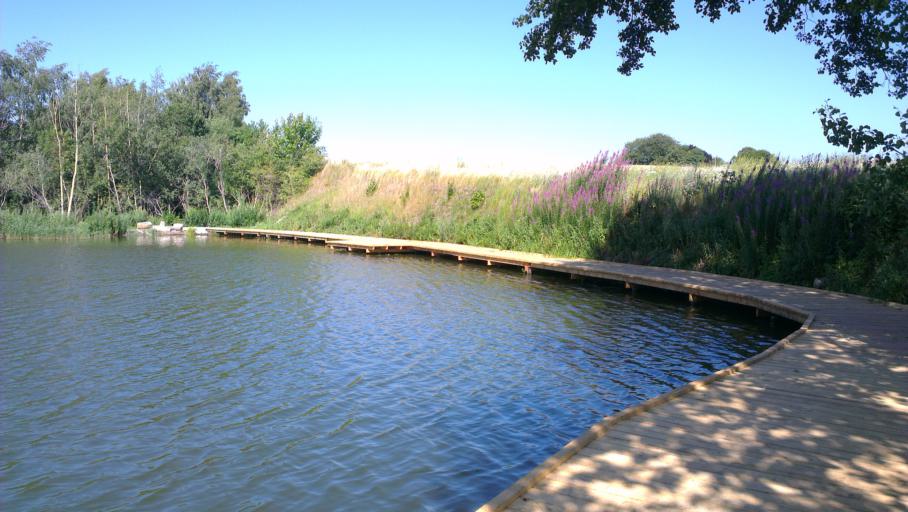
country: DK
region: Capital Region
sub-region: Frederikssund Kommune
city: Frederikssund
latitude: 55.8319
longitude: 12.0920
